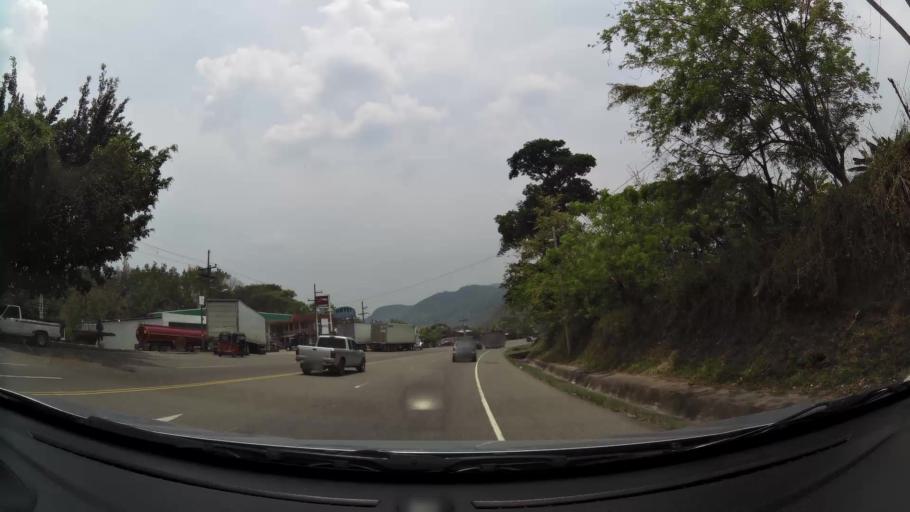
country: HN
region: Comayagua
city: Taulabe
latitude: 14.6957
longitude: -87.9615
